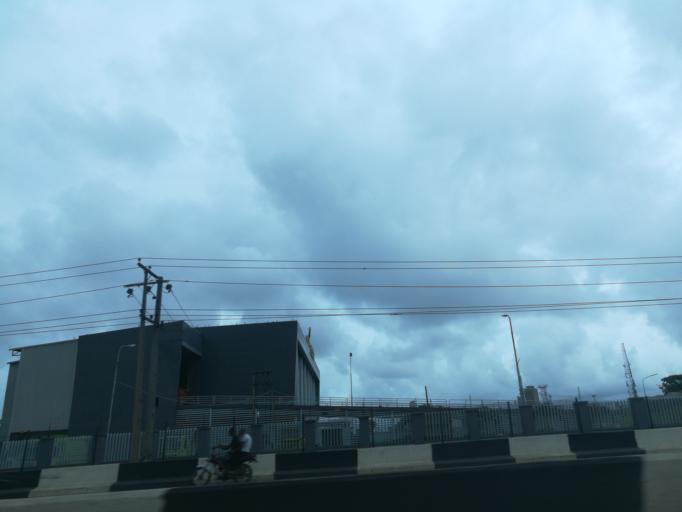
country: NG
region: Lagos
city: Lagos
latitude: 6.4585
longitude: 3.4028
